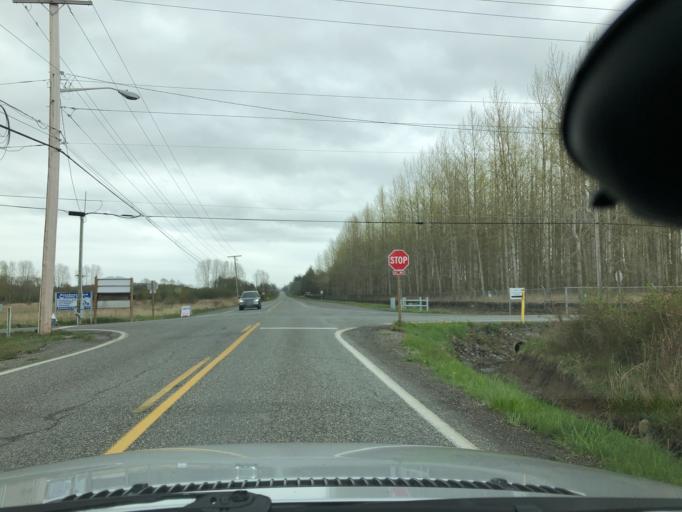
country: US
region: Washington
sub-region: Whatcom County
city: Birch Bay
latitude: 48.8923
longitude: -122.7494
